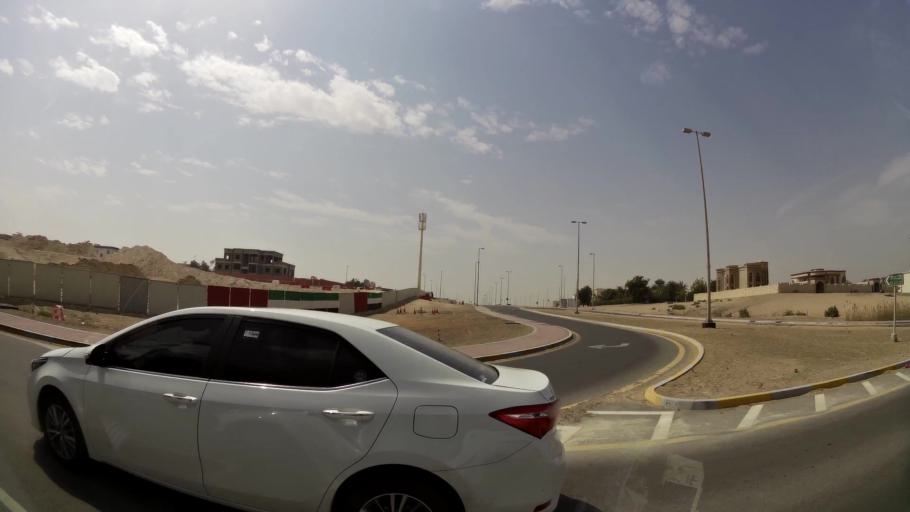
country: AE
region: Abu Dhabi
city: Abu Dhabi
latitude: 24.3112
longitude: 54.6124
